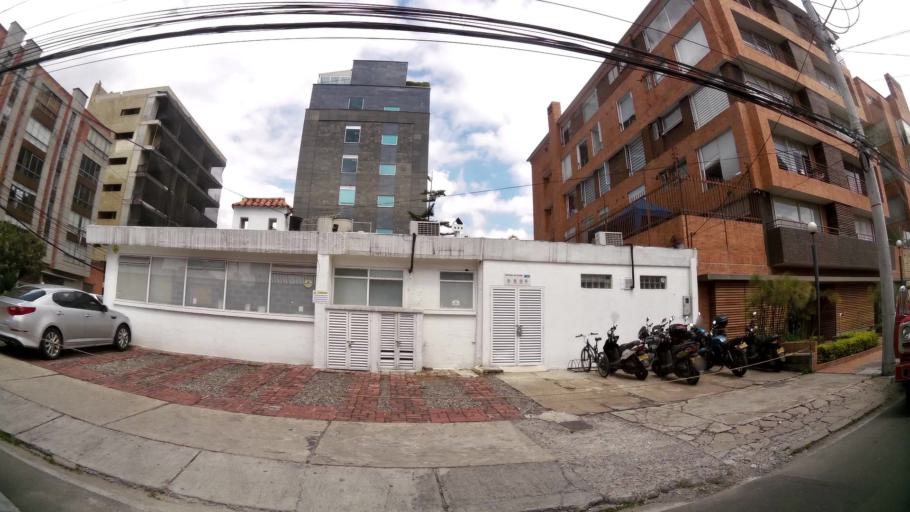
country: CO
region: Bogota D.C.
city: Barrio San Luis
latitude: 4.7027
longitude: -74.0534
